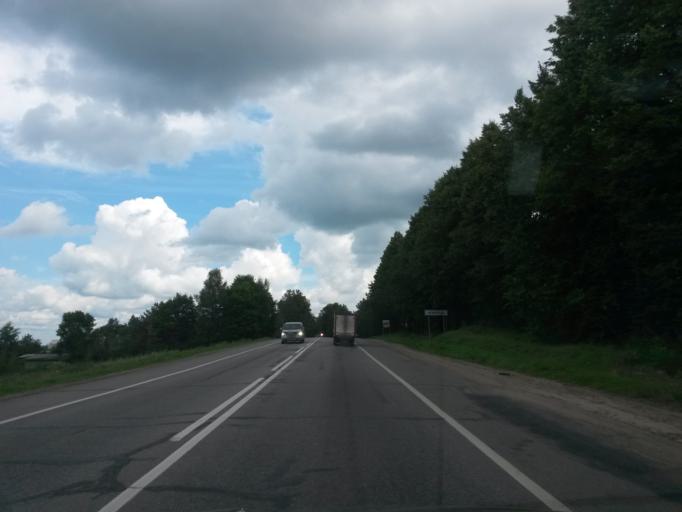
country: RU
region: Vladimir
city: Strunino
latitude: 56.5683
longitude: 38.5893
